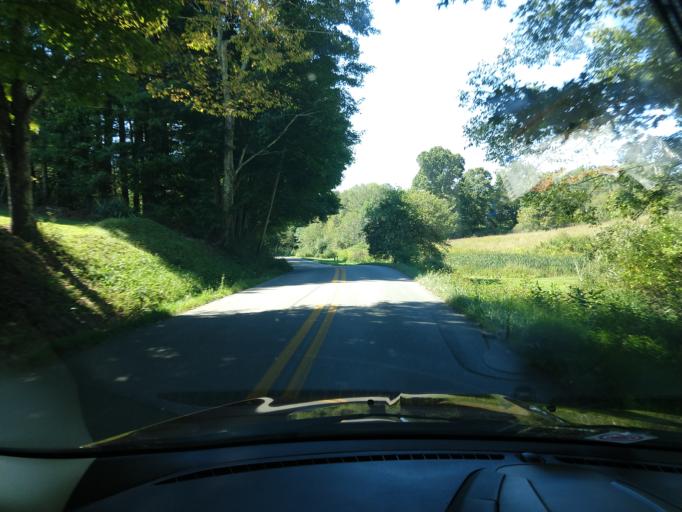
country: US
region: West Virginia
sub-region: Nicholas County
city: Summersville
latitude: 38.2718
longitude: -80.7731
